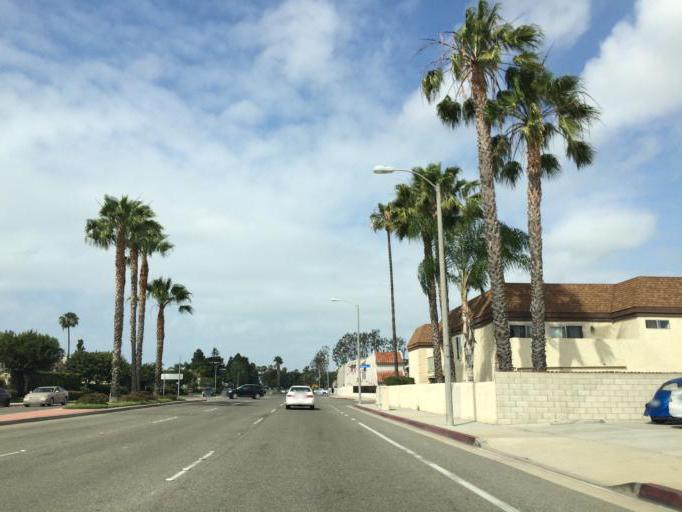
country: US
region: California
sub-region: Orange County
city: Westminster
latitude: 33.7154
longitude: -118.0438
